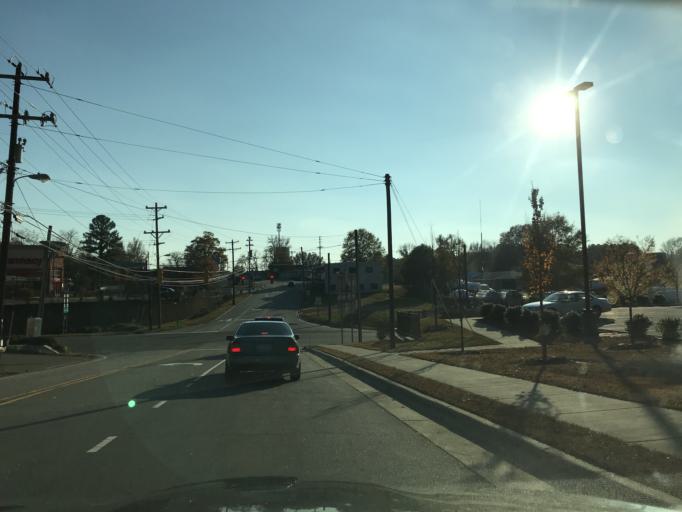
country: US
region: North Carolina
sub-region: Granville County
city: Creedmoor
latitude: 36.1231
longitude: -78.6856
